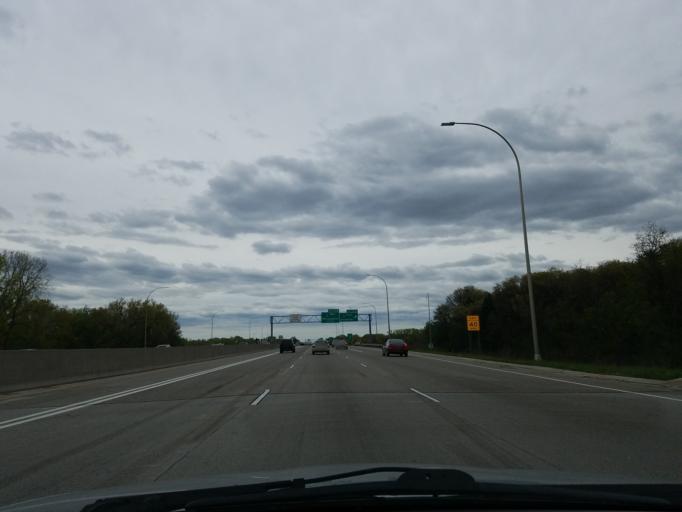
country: US
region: Minnesota
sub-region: Ramsey County
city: Little Canada
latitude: 45.0062
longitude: -93.0895
